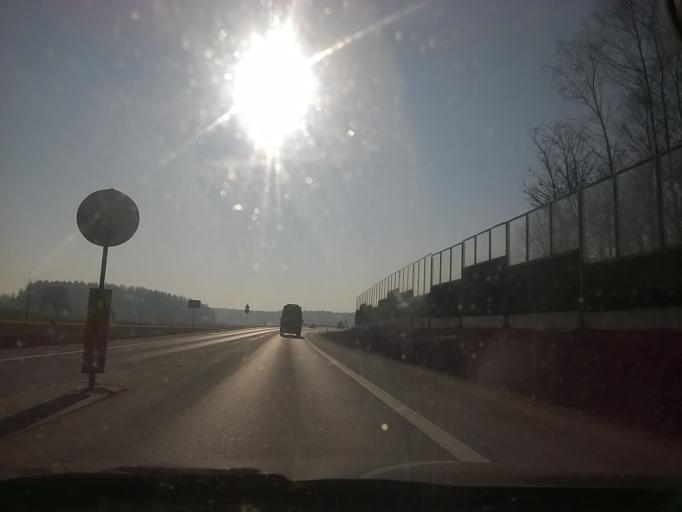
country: PL
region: Warmian-Masurian Voivodeship
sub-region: Powiat olsztynski
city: Barczewo
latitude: 53.7911
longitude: 20.6067
